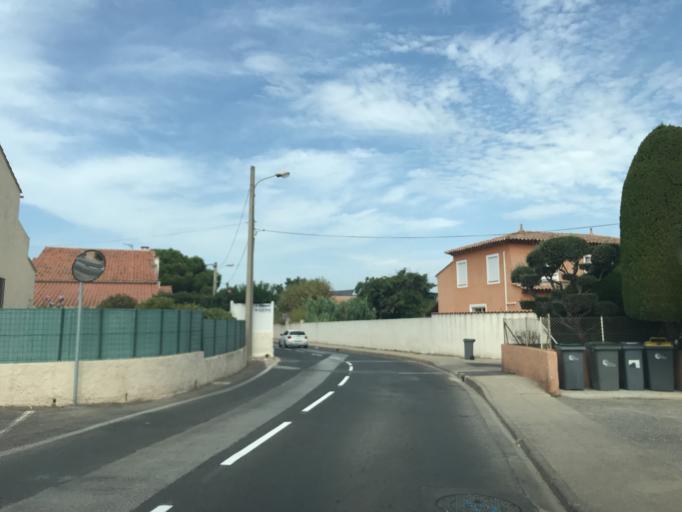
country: FR
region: Provence-Alpes-Cote d'Azur
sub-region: Departement du Var
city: Six-Fours-les-Plages
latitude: 43.0950
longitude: 5.8298
